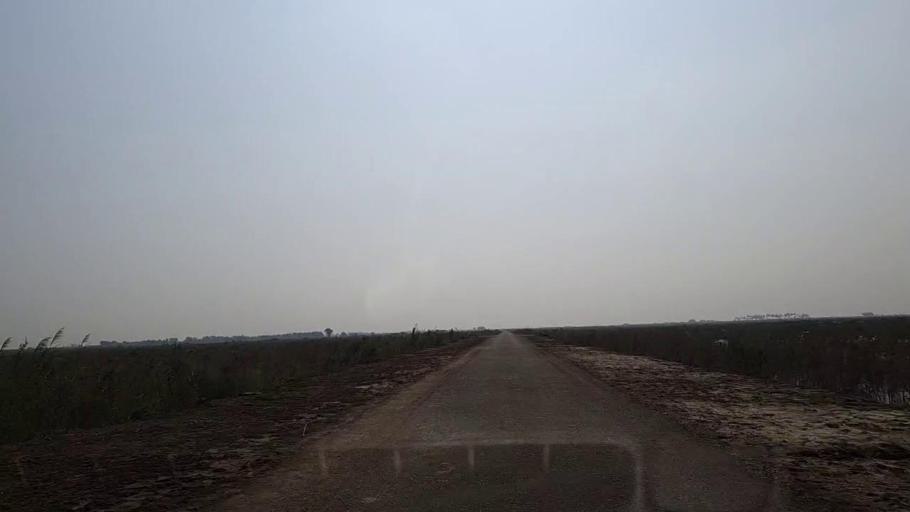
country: PK
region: Sindh
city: Gharo
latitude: 24.6665
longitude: 67.6948
